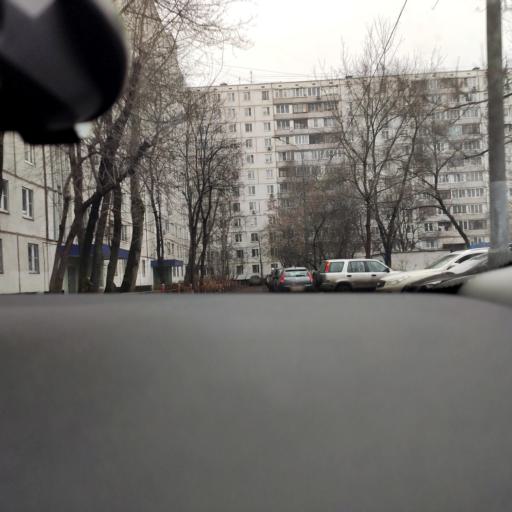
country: RU
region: Moscow
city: Bibirevo
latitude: 55.8821
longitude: 37.5957
